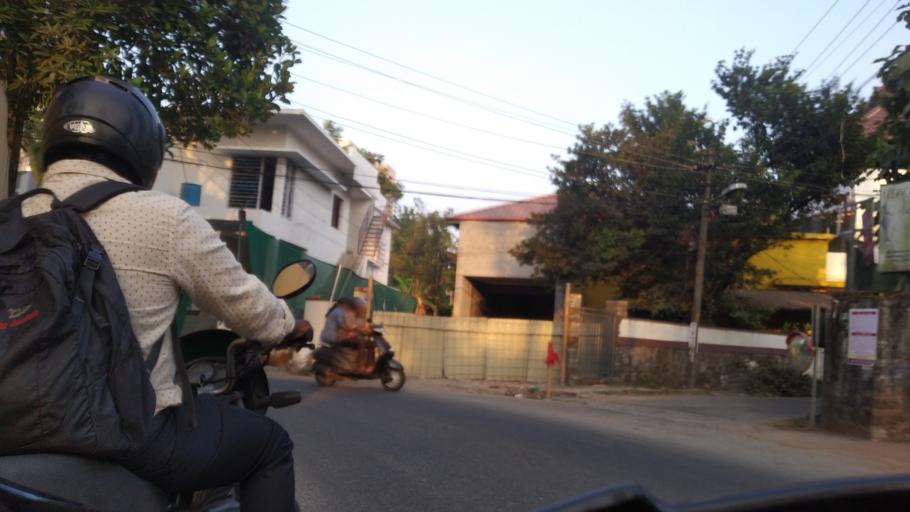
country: IN
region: Kerala
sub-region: Ernakulam
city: Elur
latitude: 10.0322
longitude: 76.2757
